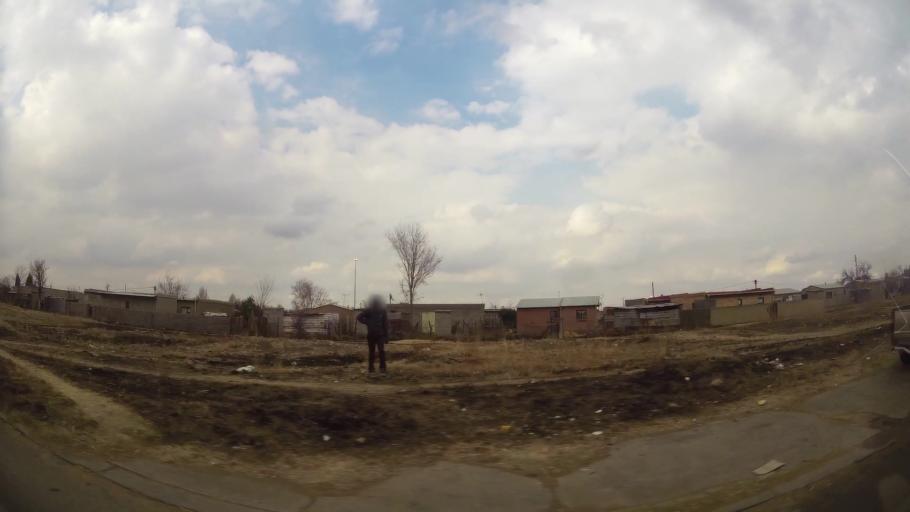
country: ZA
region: Orange Free State
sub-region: Fezile Dabi District Municipality
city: Sasolburg
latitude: -26.8521
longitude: 27.8741
